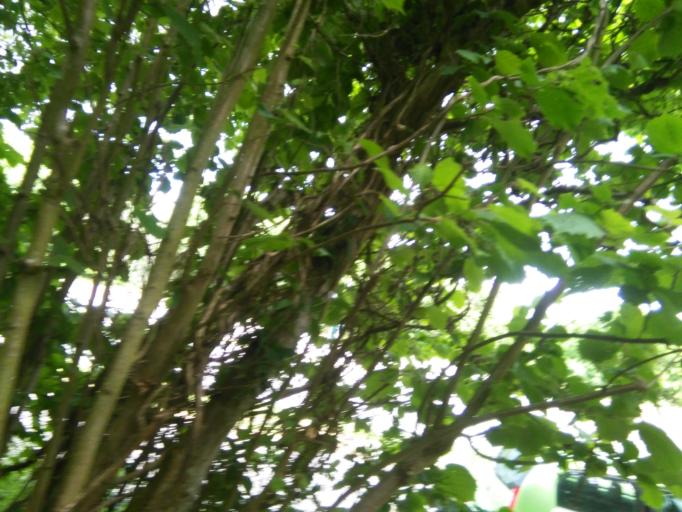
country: DK
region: Capital Region
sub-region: Bornholm Kommune
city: Akirkeby
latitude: 55.2377
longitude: 14.8713
